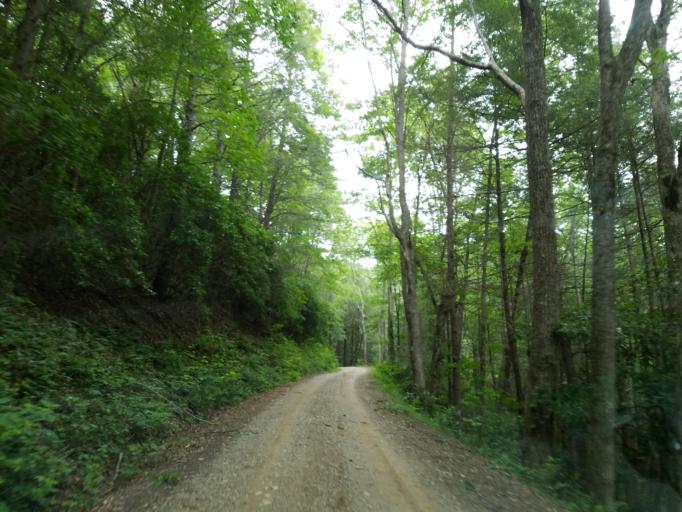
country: US
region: Georgia
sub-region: Union County
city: Blairsville
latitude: 34.7725
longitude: -84.0555
